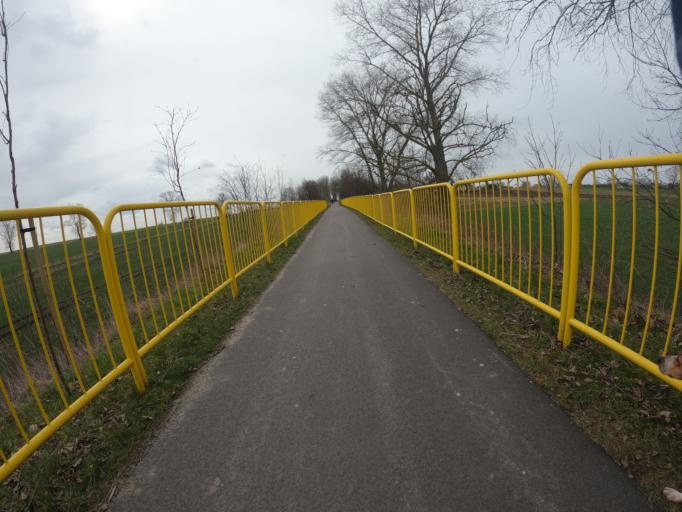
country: PL
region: West Pomeranian Voivodeship
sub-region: Powiat gryficki
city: Trzebiatow
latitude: 54.0924
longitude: 15.2730
